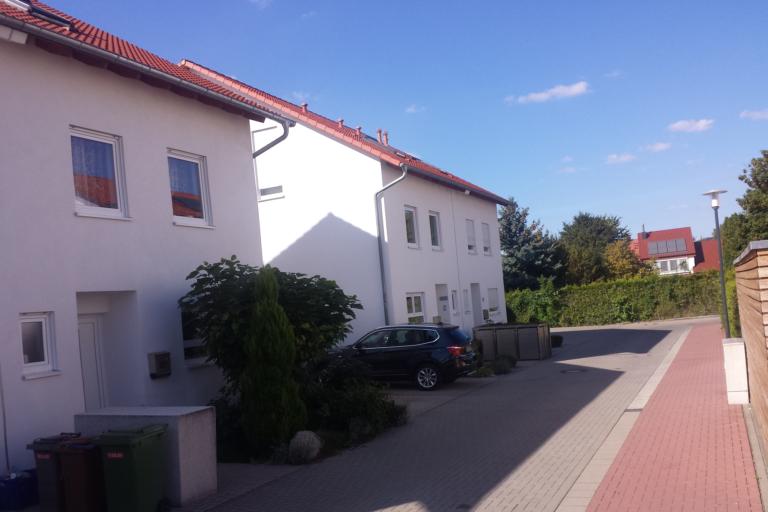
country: DE
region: Baden-Wuerttemberg
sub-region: Karlsruhe Region
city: Hemsbach
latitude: 49.5968
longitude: 8.6398
